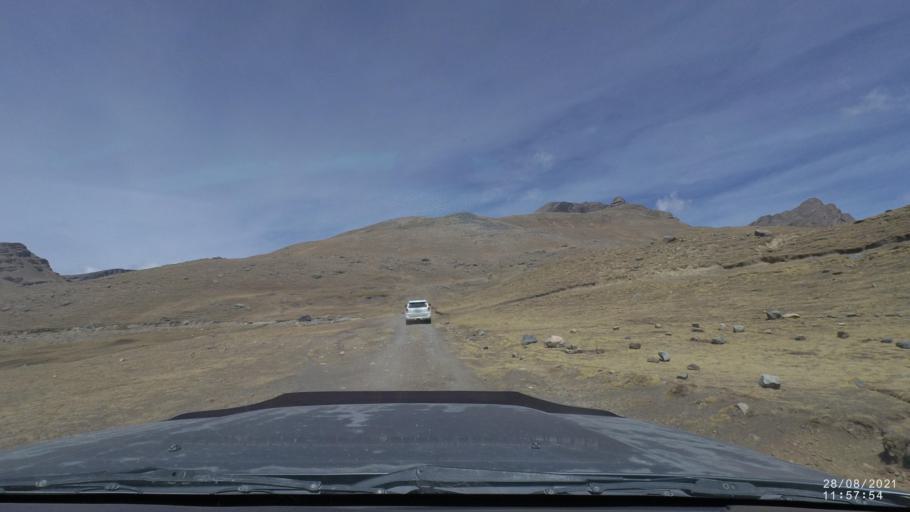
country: BO
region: Cochabamba
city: Sipe Sipe
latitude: -17.2560
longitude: -66.3885
